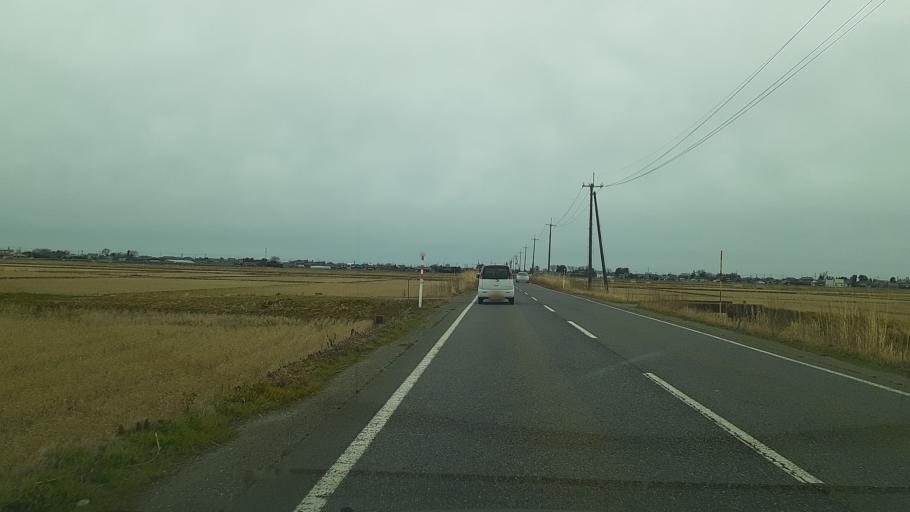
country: JP
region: Niigata
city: Niitsu-honcho
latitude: 37.8273
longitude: 139.0836
